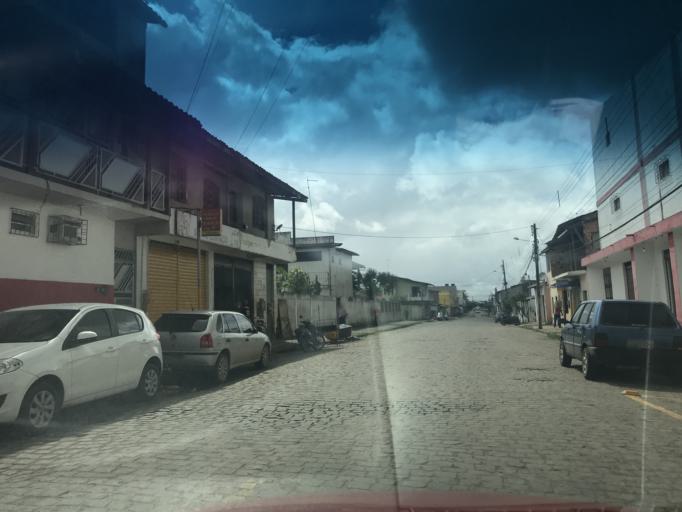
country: BR
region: Bahia
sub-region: Cruz Das Almas
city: Cruz das Almas
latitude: -12.6776
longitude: -39.0991
